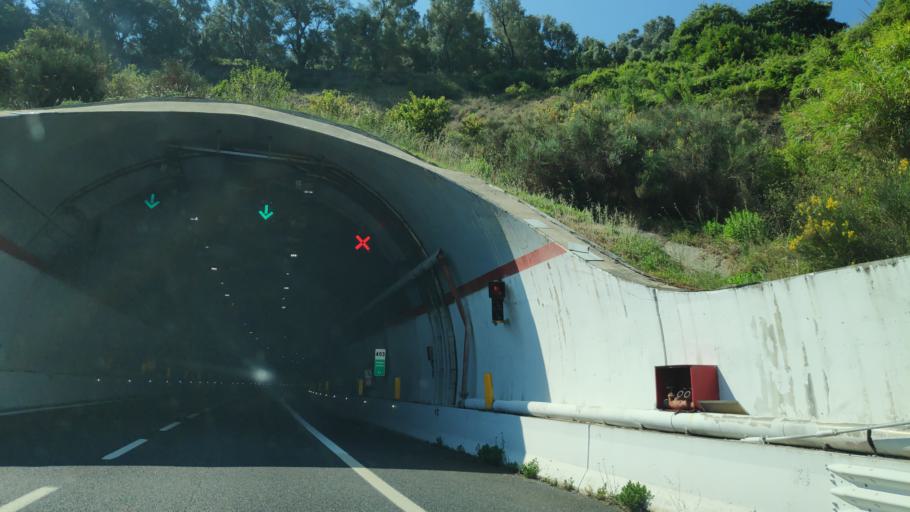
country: IT
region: Calabria
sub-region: Provincia di Reggio Calabria
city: Seminara
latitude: 38.3535
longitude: 15.8684
